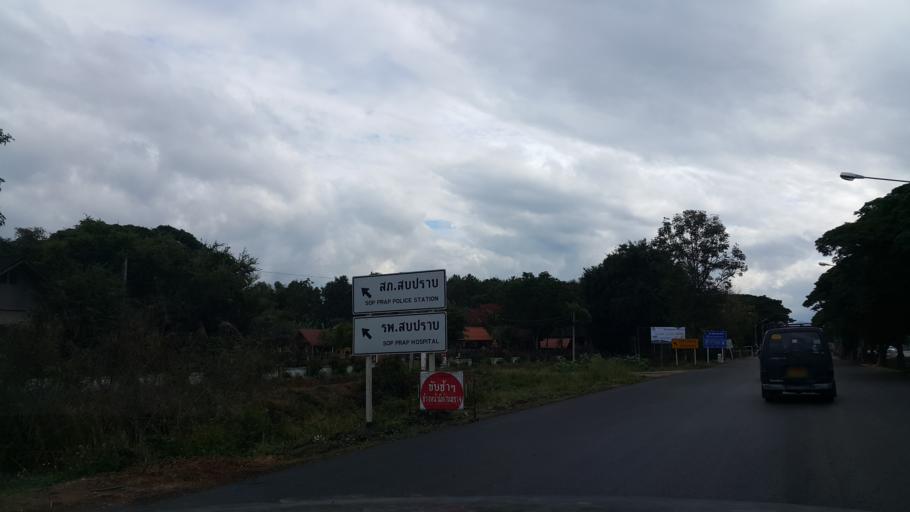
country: TH
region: Lampang
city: Sop Prap
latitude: 17.9019
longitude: 99.3414
